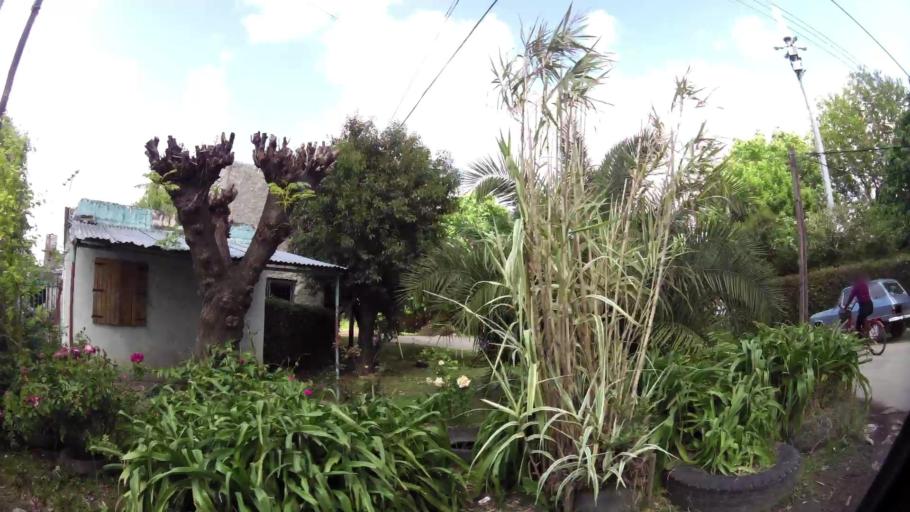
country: AR
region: Buenos Aires
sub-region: Partido de Quilmes
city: Quilmes
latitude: -34.8273
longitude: -58.1849
